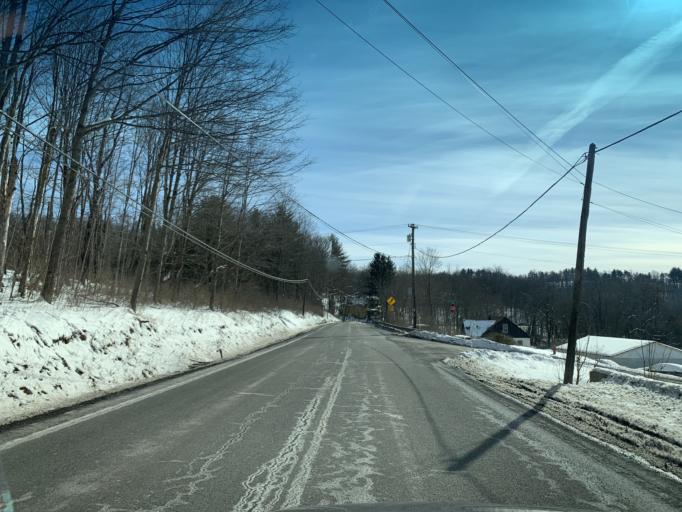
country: US
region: Maryland
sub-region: Allegany County
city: Lonaconing
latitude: 39.6020
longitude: -78.9449
